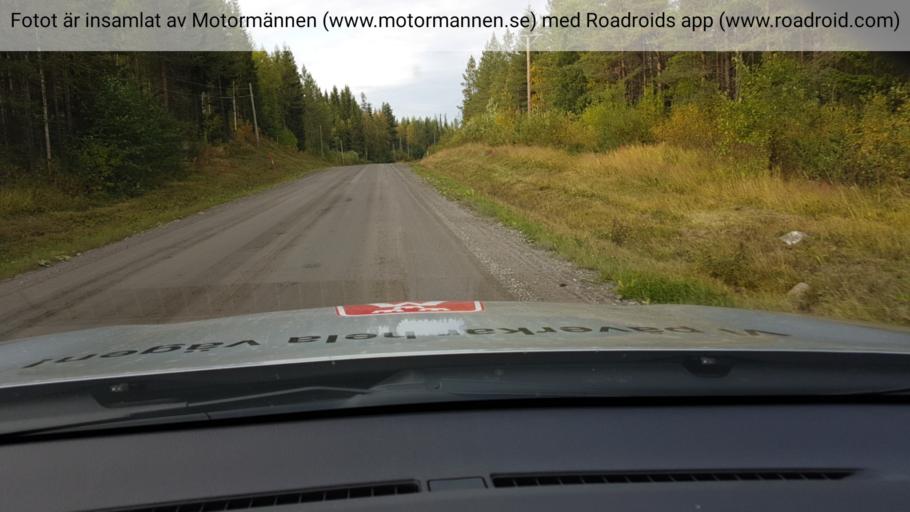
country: SE
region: Jaemtland
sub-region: Stroemsunds Kommun
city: Stroemsund
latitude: 63.9747
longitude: 15.8236
